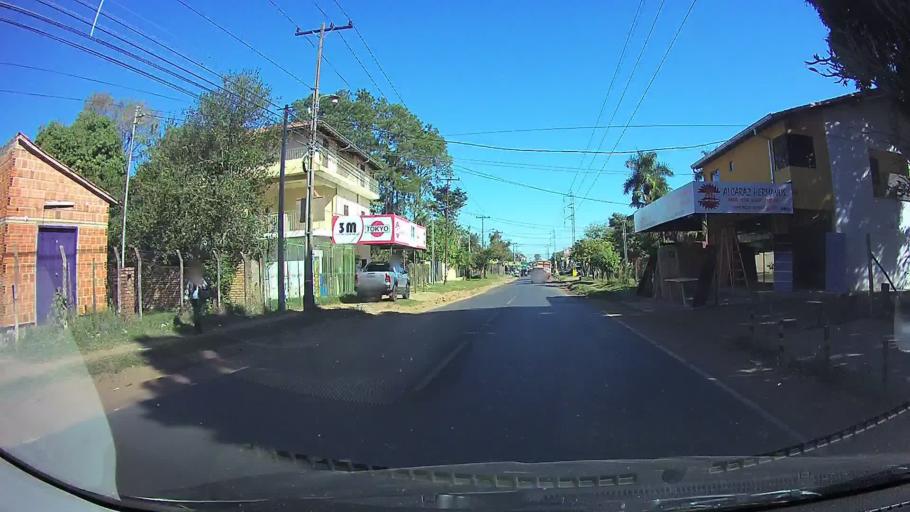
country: PY
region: Central
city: Fernando de la Mora
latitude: -25.3568
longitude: -57.5469
